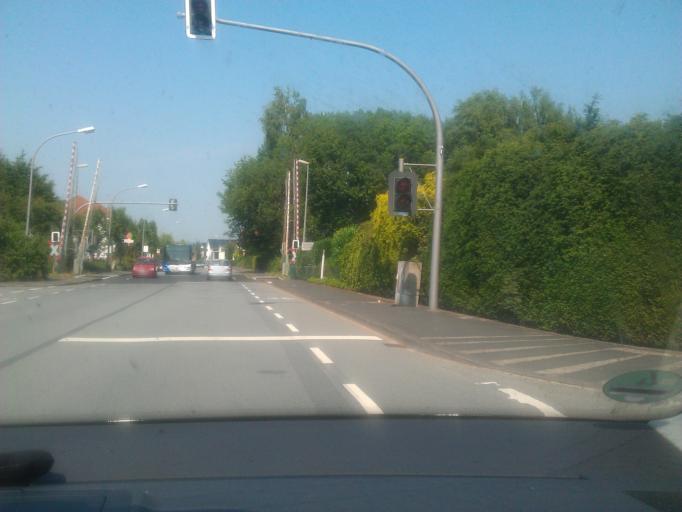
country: DE
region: North Rhine-Westphalia
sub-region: Regierungsbezirk Detmold
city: Oerlinghausen
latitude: 51.9775
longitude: 8.6679
